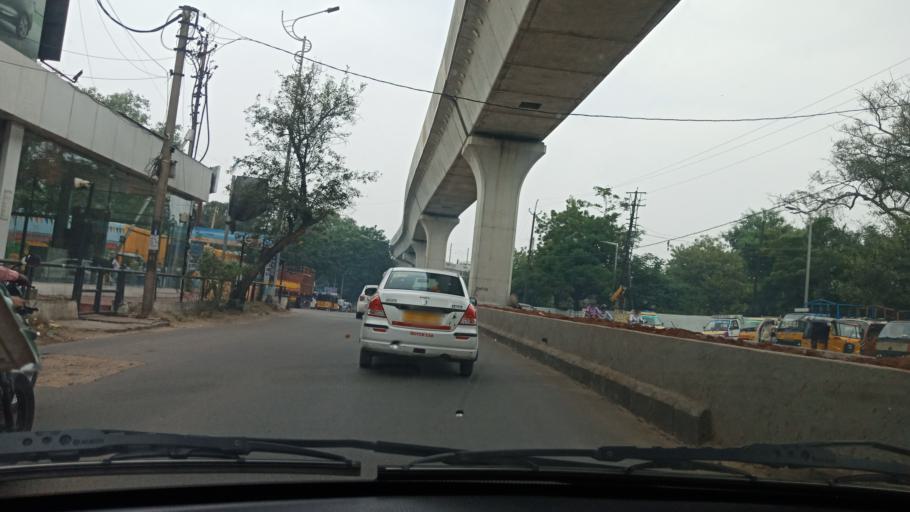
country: IN
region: Telangana
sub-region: Hyderabad
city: Malkajgiri
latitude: 17.4311
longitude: 78.5052
